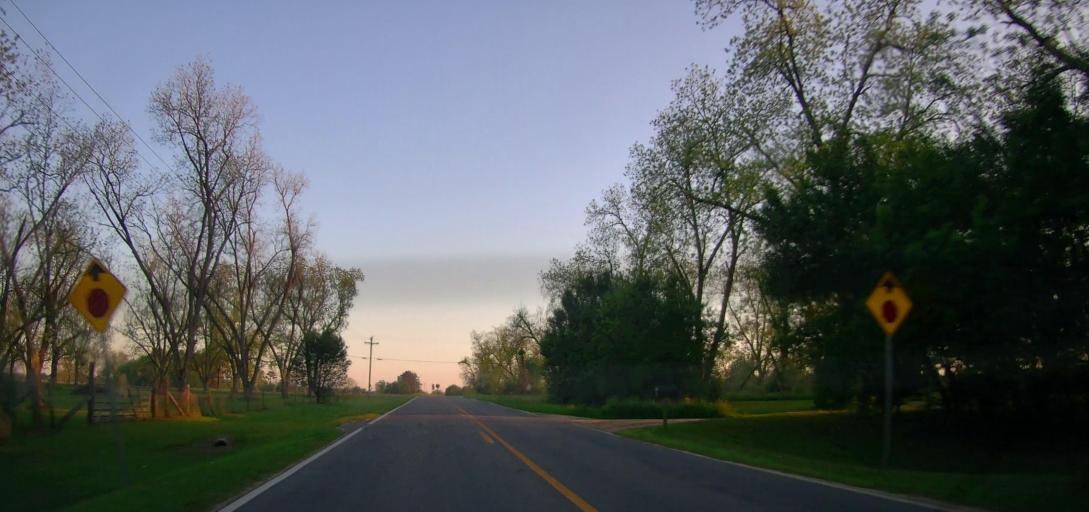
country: US
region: Georgia
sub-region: Ben Hill County
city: Fitzgerald
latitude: 31.7190
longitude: -83.3099
